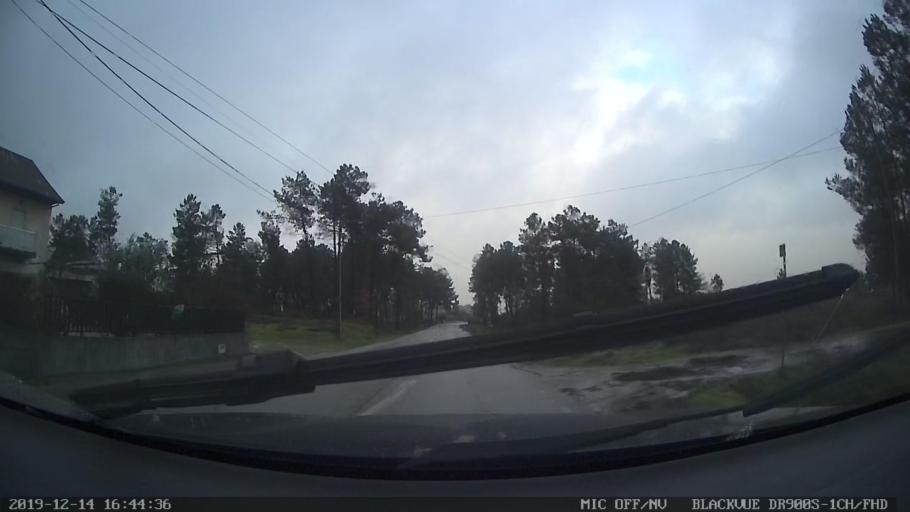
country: PT
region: Vila Real
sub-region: Murca
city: Murca
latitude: 41.3930
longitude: -7.4944
